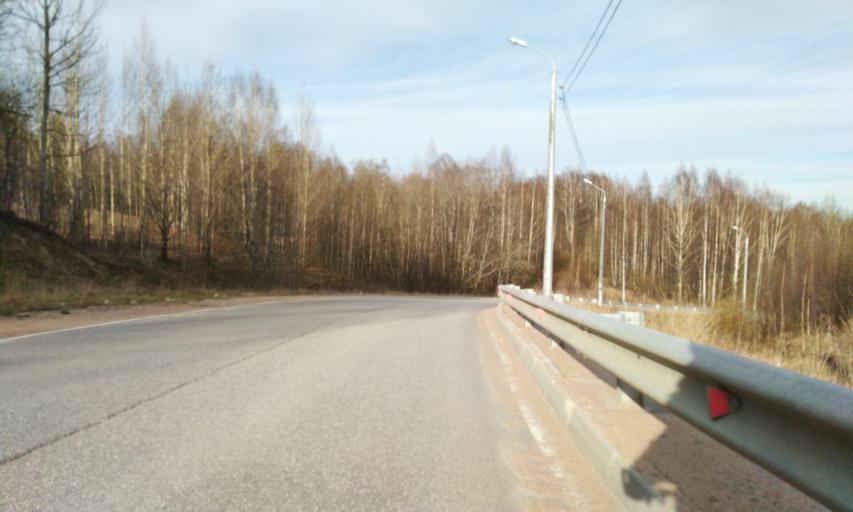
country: RU
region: Leningrad
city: Bugry
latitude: 60.1151
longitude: 30.4272
